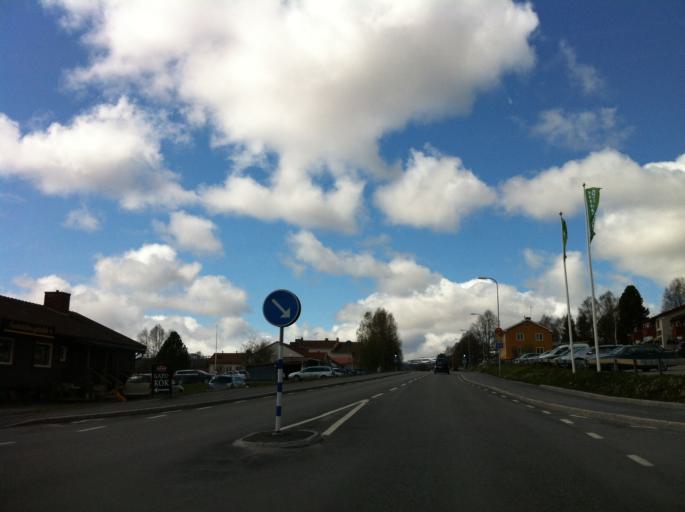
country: NO
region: Hedmark
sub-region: Engerdal
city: Engerdal
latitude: 62.5487
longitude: 12.5329
